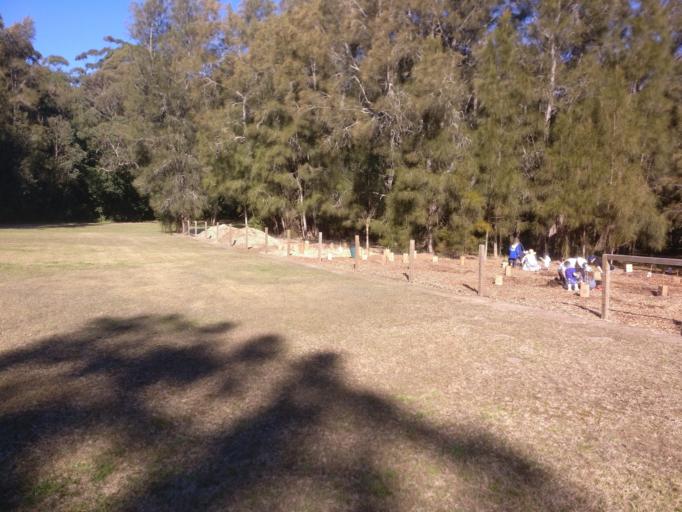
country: AU
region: New South Wales
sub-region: Warringah
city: Narrabeen
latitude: -33.7256
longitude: 151.2758
